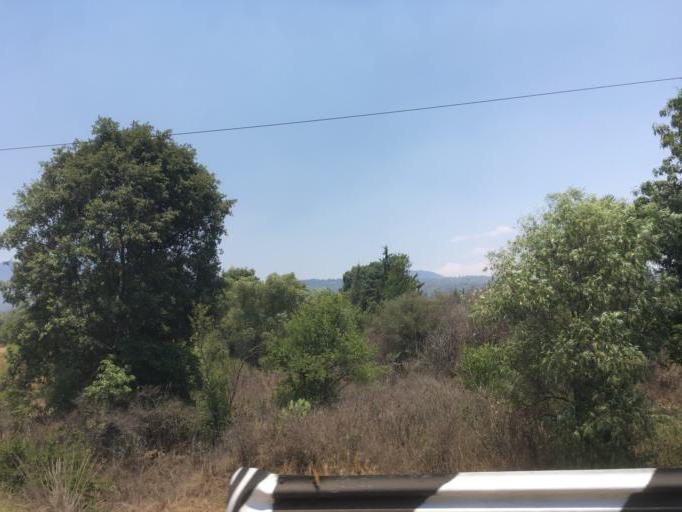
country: MX
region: Michoacan
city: Quiroga
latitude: 19.6458
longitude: -101.4911
